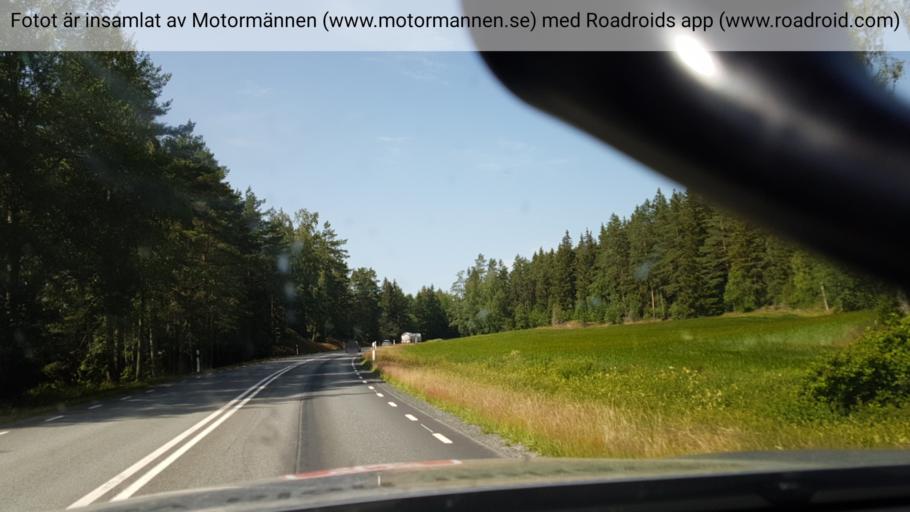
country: SE
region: Joenkoeping
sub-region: Eksjo Kommun
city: Eksjoe
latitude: 57.7455
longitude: 14.9283
